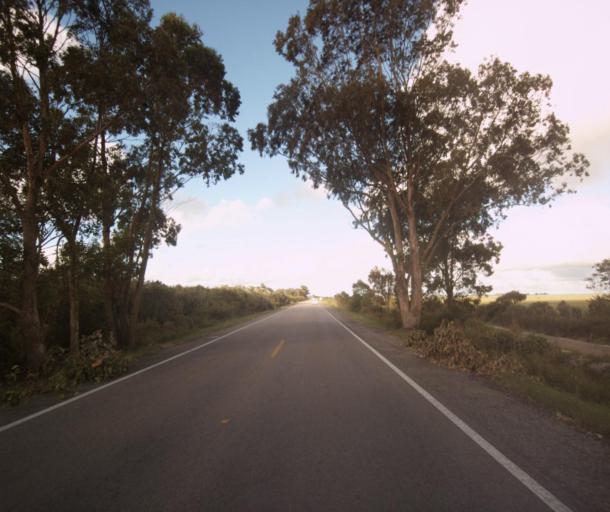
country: BR
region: Rio Grande do Sul
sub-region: Rio Grande
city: Rio Grande
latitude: -32.1884
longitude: -52.4312
